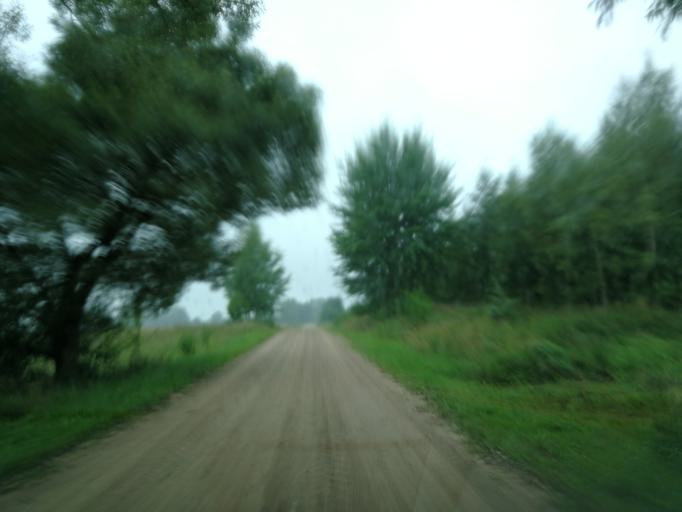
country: LV
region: Preilu Rajons
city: Jaunaglona
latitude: 56.3162
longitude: 27.0068
